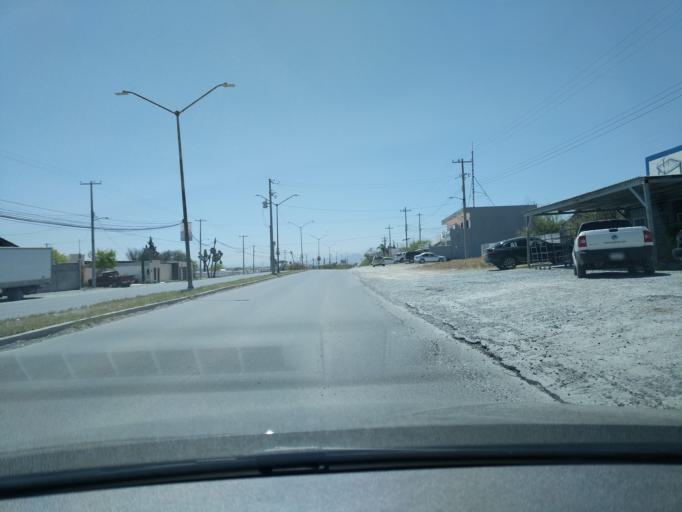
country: MX
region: Nuevo Leon
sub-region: Apodaca
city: Artemio Trevino
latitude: 25.8045
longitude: -100.1561
